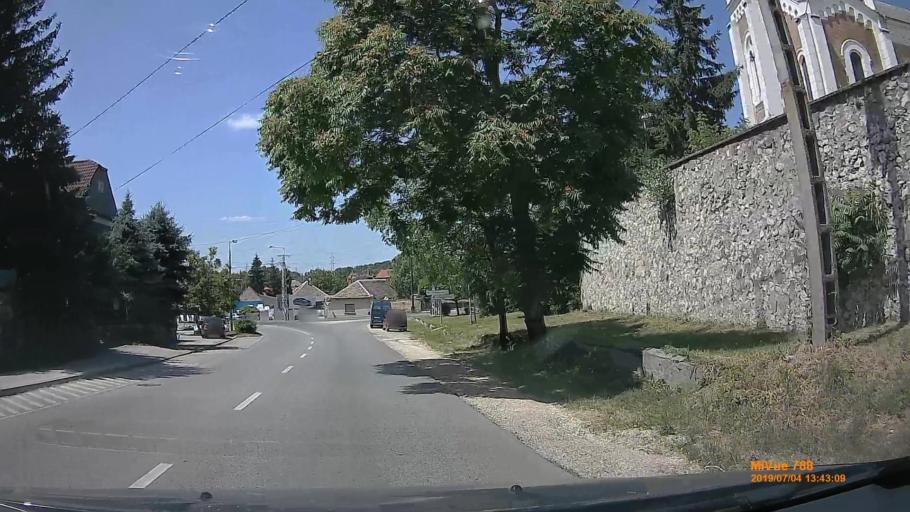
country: HU
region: Komarom-Esztergom
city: Tatabanya
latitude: 47.5749
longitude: 18.3832
